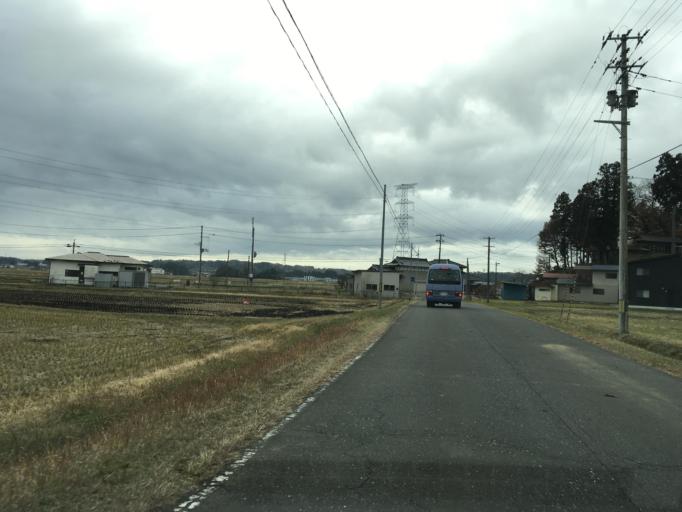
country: JP
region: Iwate
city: Ichinoseki
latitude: 38.8228
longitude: 141.0442
